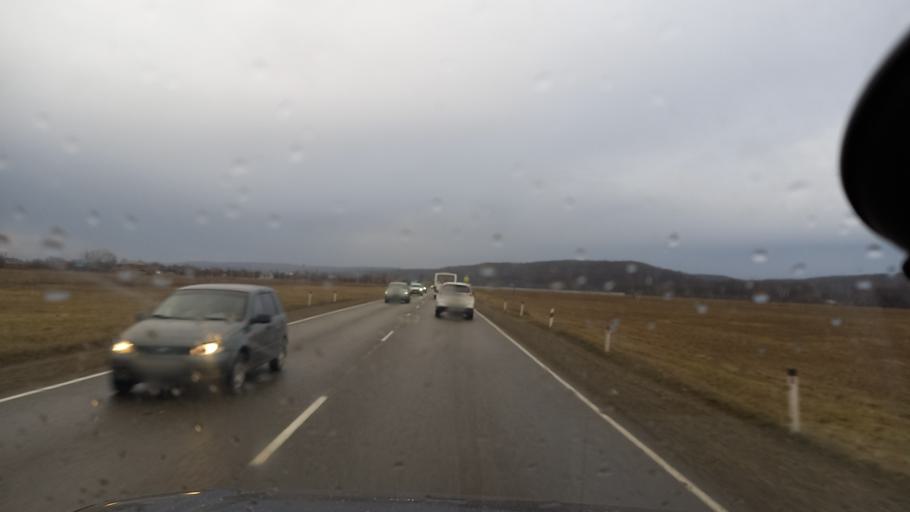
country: RU
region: Adygeya
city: Tul'skiy
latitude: 44.5350
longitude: 40.1394
